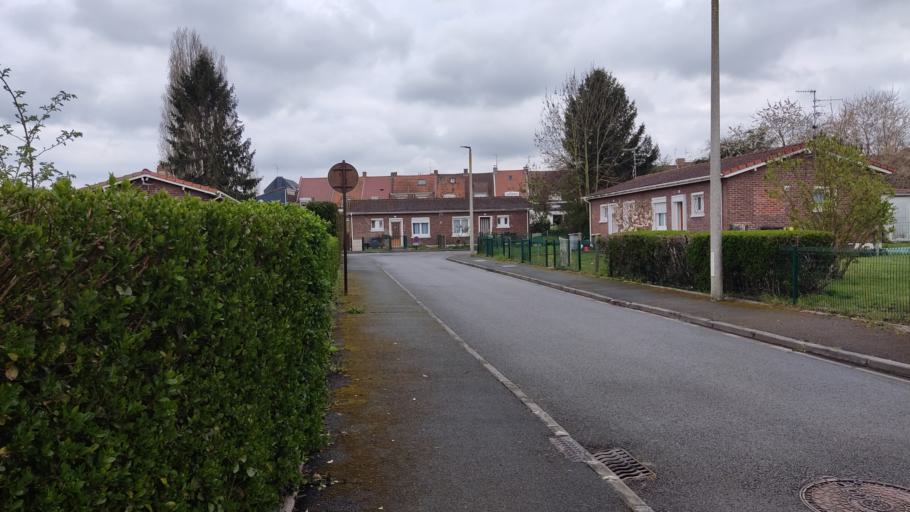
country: FR
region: Nord-Pas-de-Calais
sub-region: Departement du Pas-de-Calais
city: Montigny-en-Gohelle
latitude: 50.4207
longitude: 2.9395
